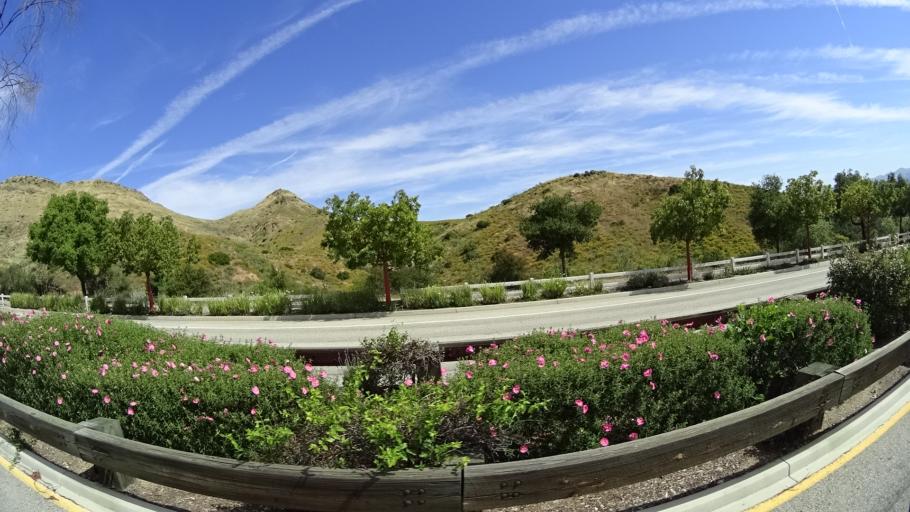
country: US
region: California
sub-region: Ventura County
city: Casa Conejo
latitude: 34.1795
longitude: -118.9651
